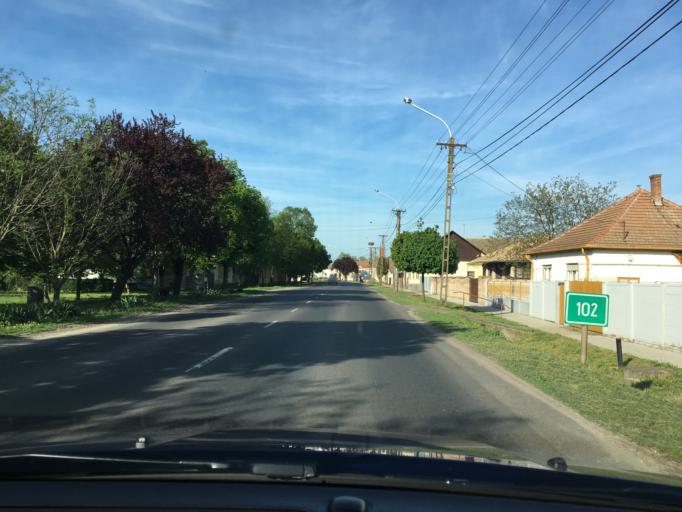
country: HU
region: Bekes
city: Korostarcsa
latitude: 46.8779
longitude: 21.0241
